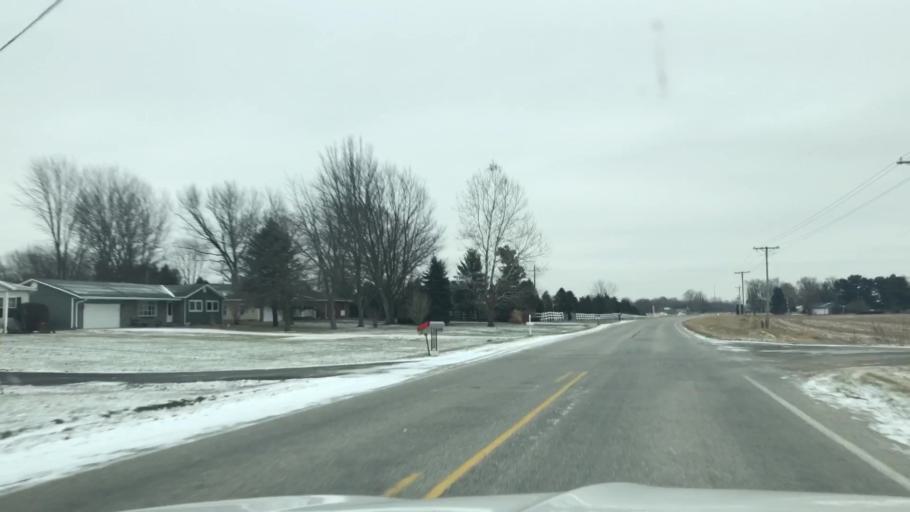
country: US
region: Indiana
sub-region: Fulton County
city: Rochester
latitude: 41.0371
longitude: -86.2001
